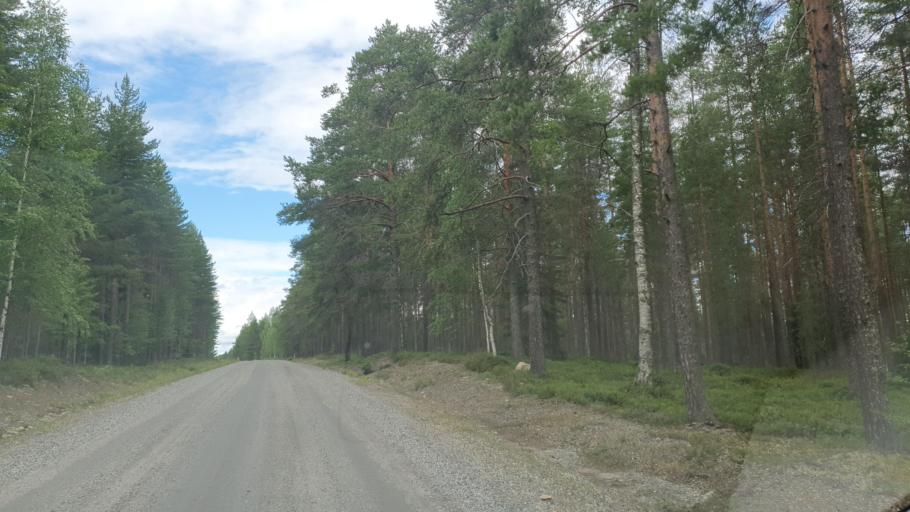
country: FI
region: Kainuu
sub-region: Kehys-Kainuu
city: Kuhmo
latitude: 64.1065
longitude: 29.3941
